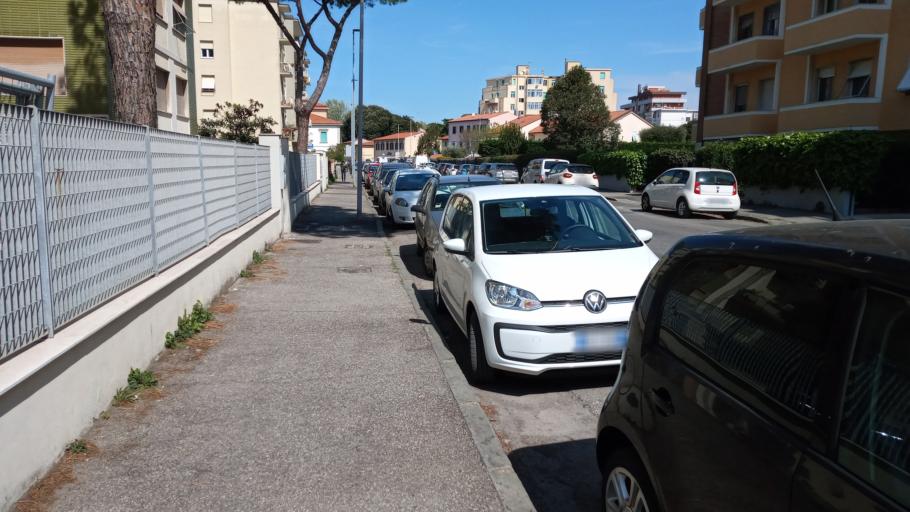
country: IT
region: Tuscany
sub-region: Provincia di Livorno
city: Livorno
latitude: 43.5328
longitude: 10.3170
